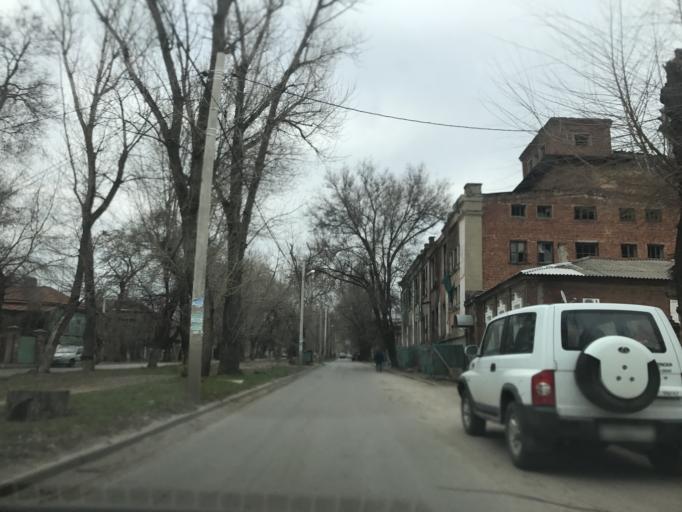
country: RU
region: Rostov
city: Novocherkassk
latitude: 47.4110
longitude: 40.0916
